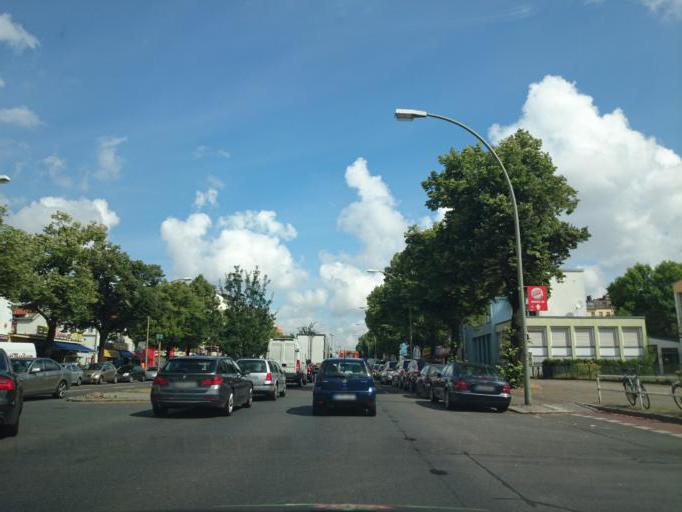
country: DE
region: Berlin
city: Tempelhof Bezirk
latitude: 52.4671
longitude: 13.3857
